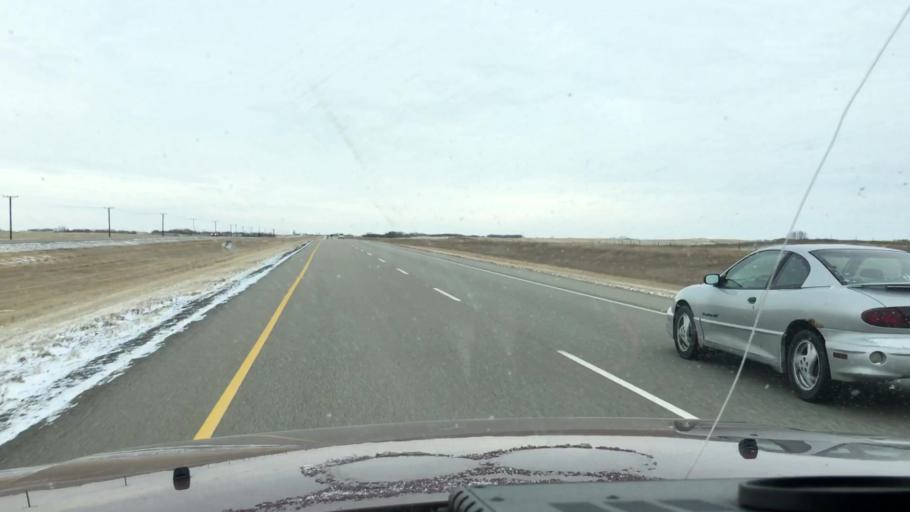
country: CA
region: Saskatchewan
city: Watrous
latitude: 51.4038
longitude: -106.1797
